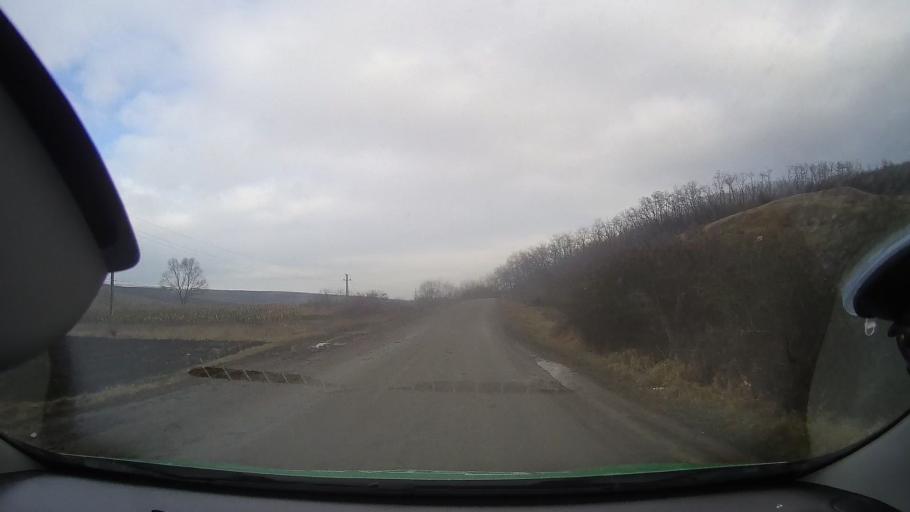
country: RO
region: Mures
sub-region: Comuna Ludus
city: Gheja
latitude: 46.4051
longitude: 24.0633
